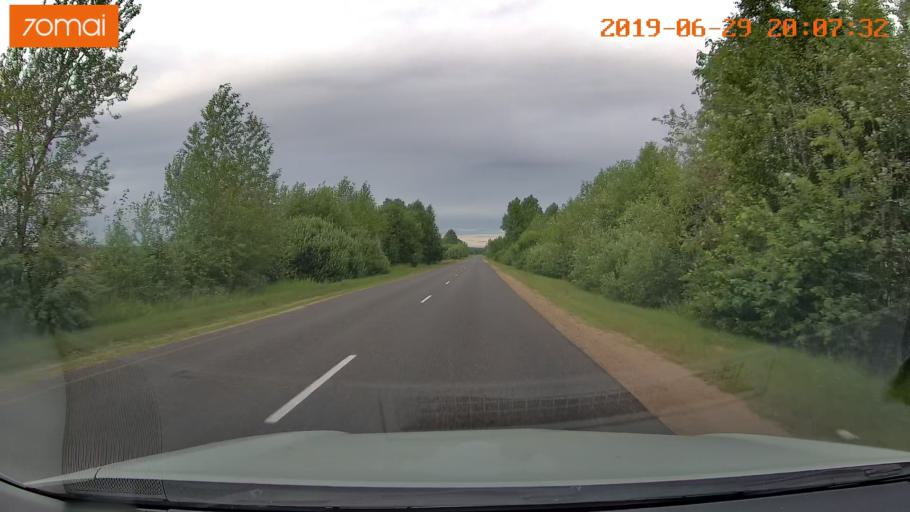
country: BY
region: Brest
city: Lahishyn
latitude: 52.3413
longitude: 26.0381
